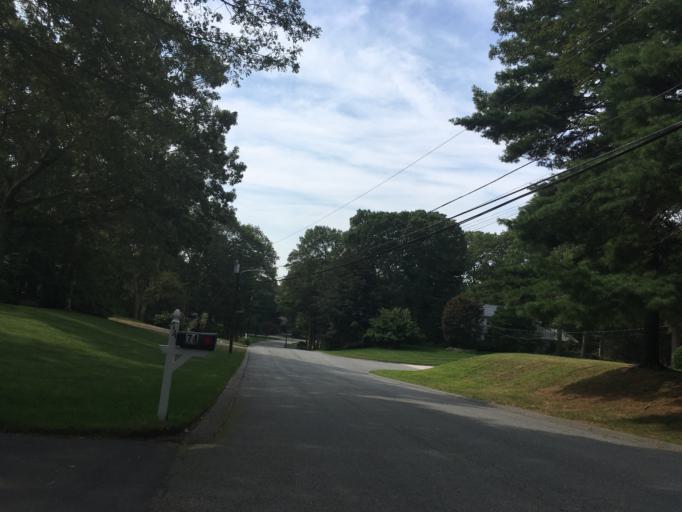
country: US
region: Rhode Island
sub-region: Kent County
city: East Greenwich
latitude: 41.6361
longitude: -71.4780
